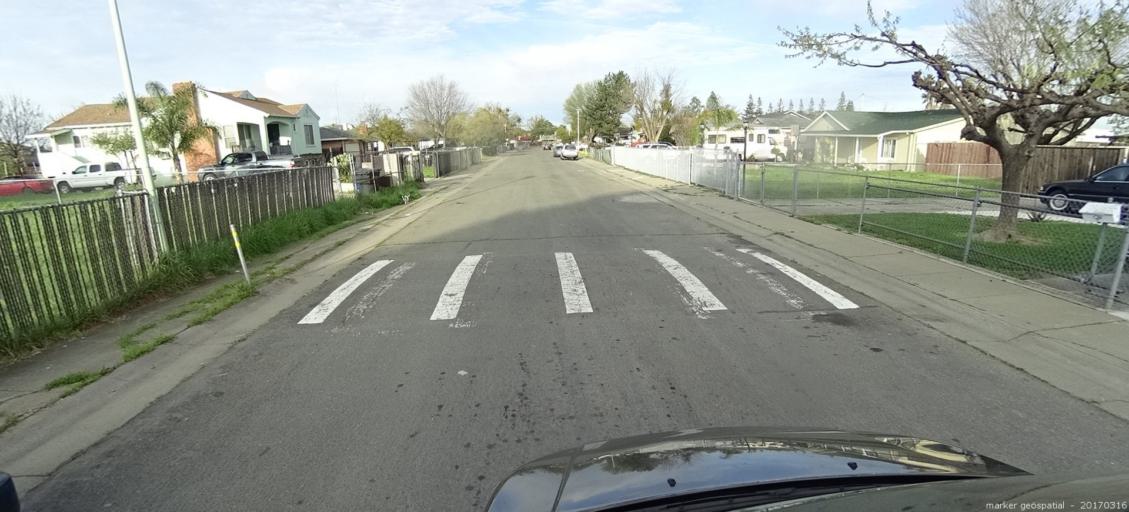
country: US
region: California
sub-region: Sacramento County
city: Parkway
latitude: 38.5069
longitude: -121.4806
